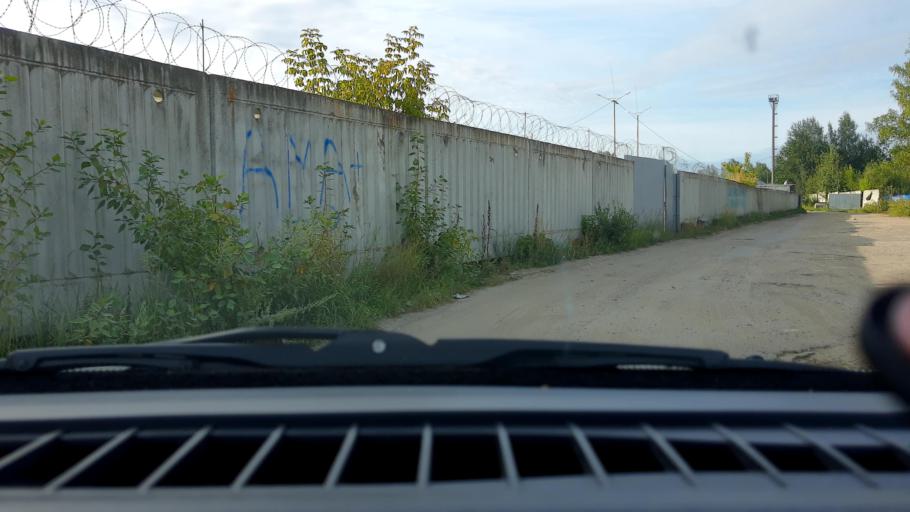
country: RU
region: Nizjnij Novgorod
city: Gorbatovka
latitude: 56.3543
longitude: 43.7893
